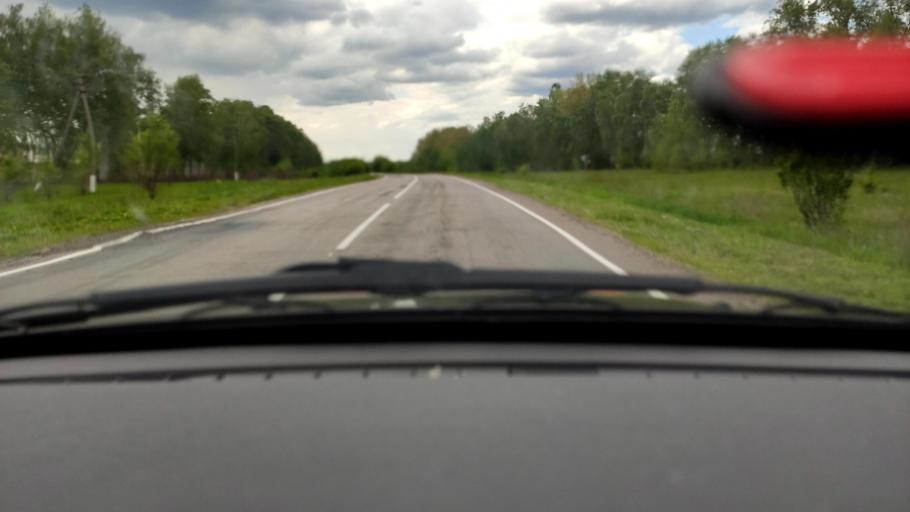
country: RU
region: Belgorod
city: Krasnoye
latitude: 51.0564
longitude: 38.8980
